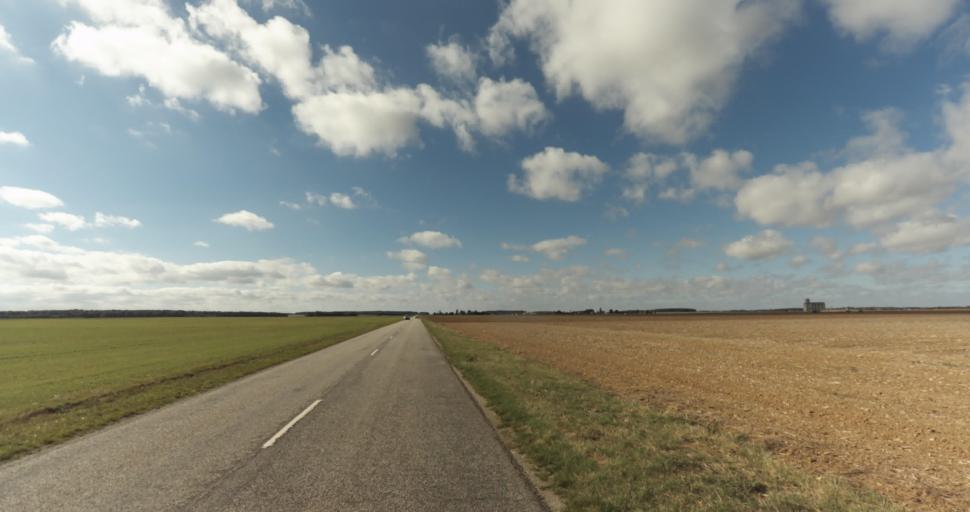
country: FR
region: Centre
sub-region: Departement d'Eure-et-Loir
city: Garnay
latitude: 48.7087
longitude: 1.3044
